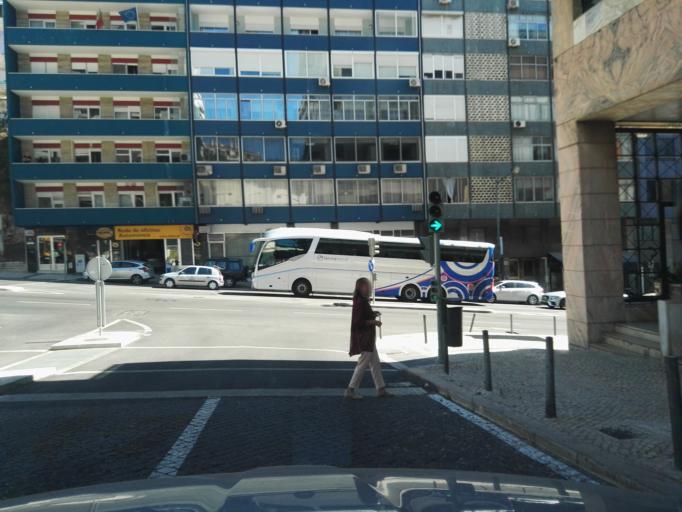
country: PT
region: Setubal
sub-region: Almada
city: Cacilhas
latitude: 38.7068
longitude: -9.1679
